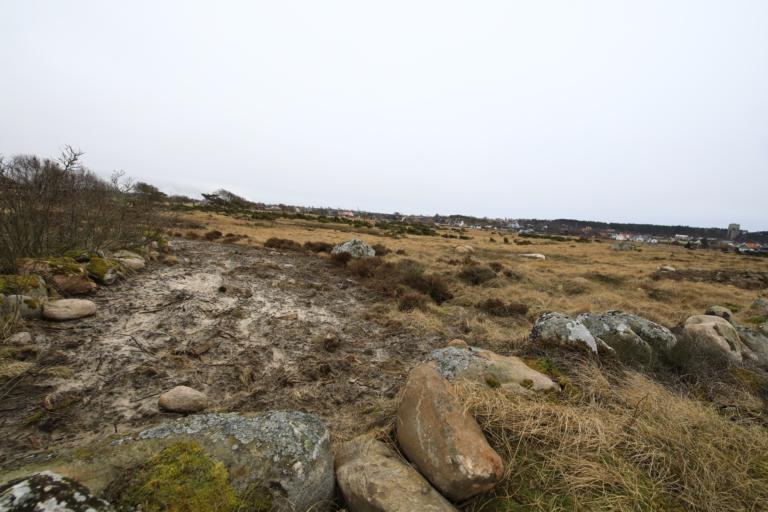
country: SE
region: Halland
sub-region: Kungsbacka Kommun
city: Frillesas
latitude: 57.2436
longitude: 12.1208
